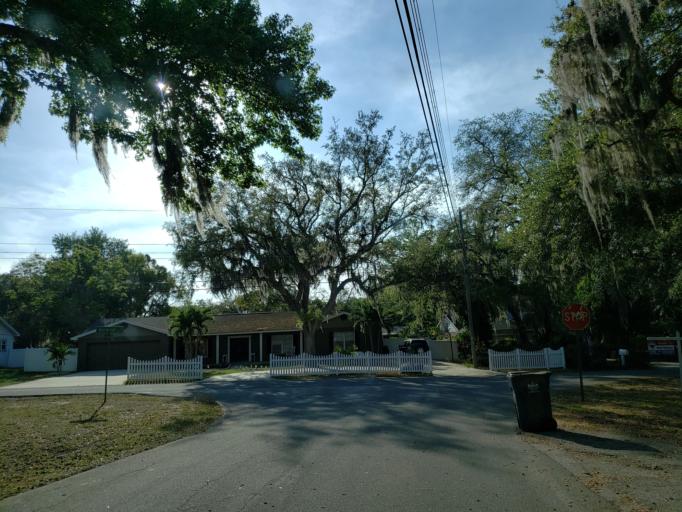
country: US
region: Florida
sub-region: Hillsborough County
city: Brandon
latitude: 27.9069
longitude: -82.2891
